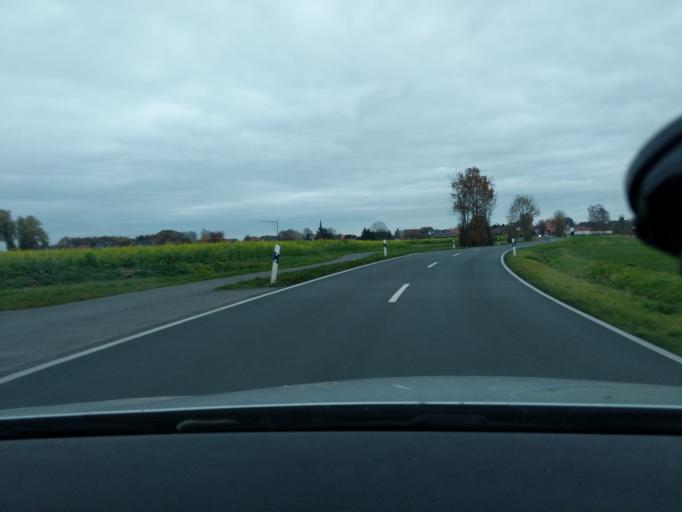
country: DE
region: North Rhine-Westphalia
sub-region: Regierungsbezirk Munster
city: Senden
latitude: 51.8283
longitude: 7.5277
